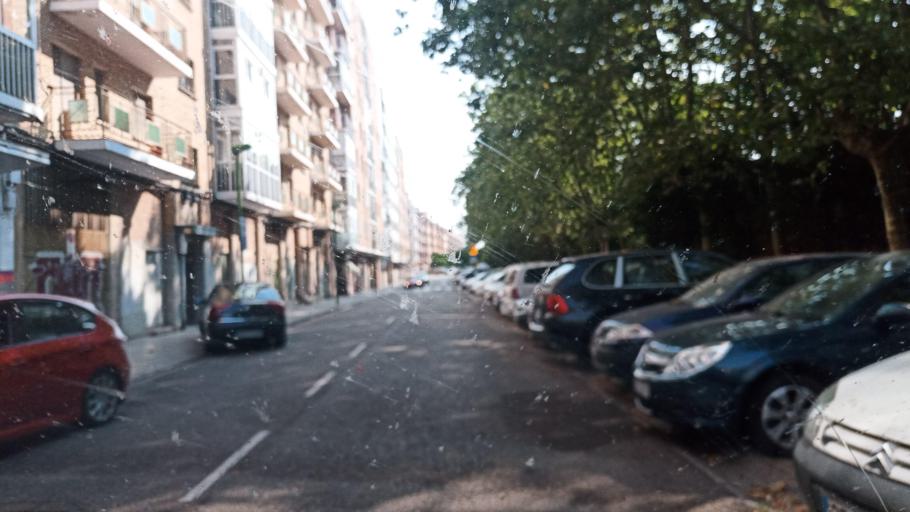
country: ES
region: Castille and Leon
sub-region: Provincia de Burgos
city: Burgos
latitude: 42.3337
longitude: -3.6960
